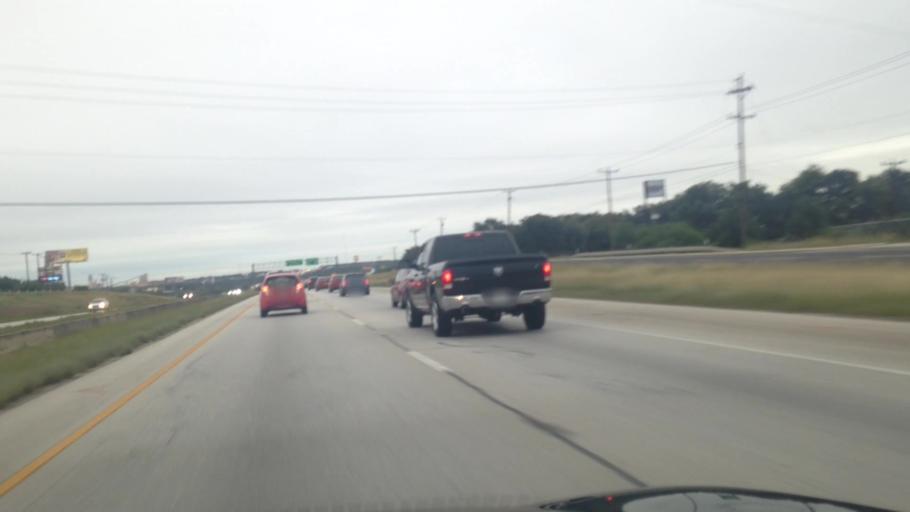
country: US
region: Texas
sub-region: Bexar County
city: Hollywood Park
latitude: 29.6000
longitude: -98.4275
